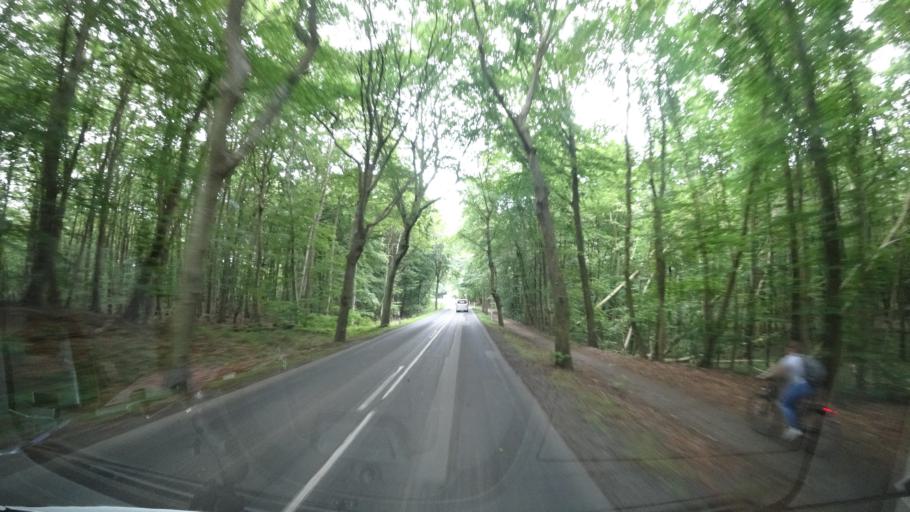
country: DE
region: Mecklenburg-Vorpommern
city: Putbus
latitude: 54.3483
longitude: 13.4488
